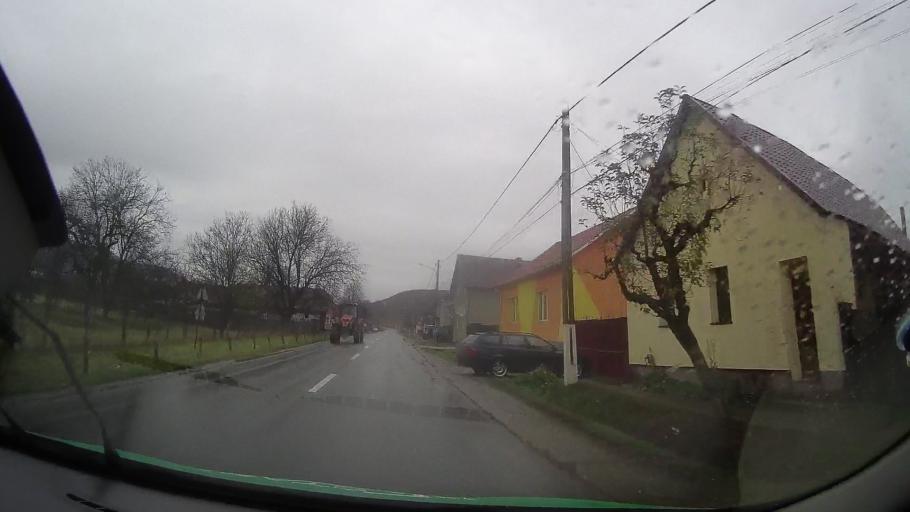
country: RO
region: Bistrita-Nasaud
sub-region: Comuna Mariselu
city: Mariselu
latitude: 47.0408
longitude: 24.4737
